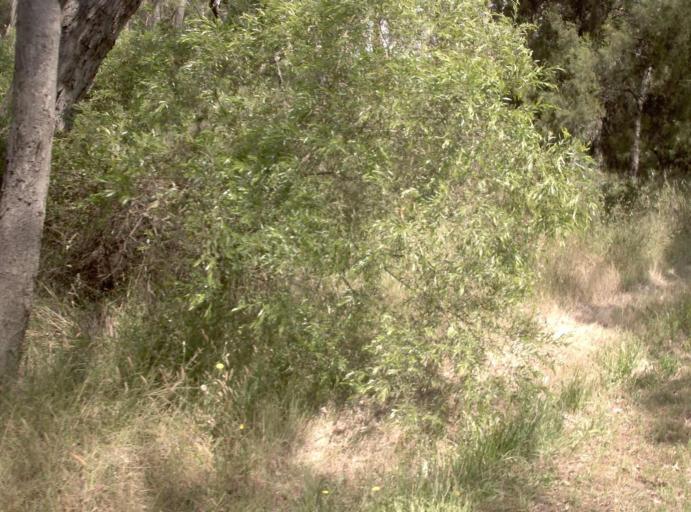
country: AU
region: Victoria
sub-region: Latrobe
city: Traralgon
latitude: -38.2941
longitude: 146.5386
